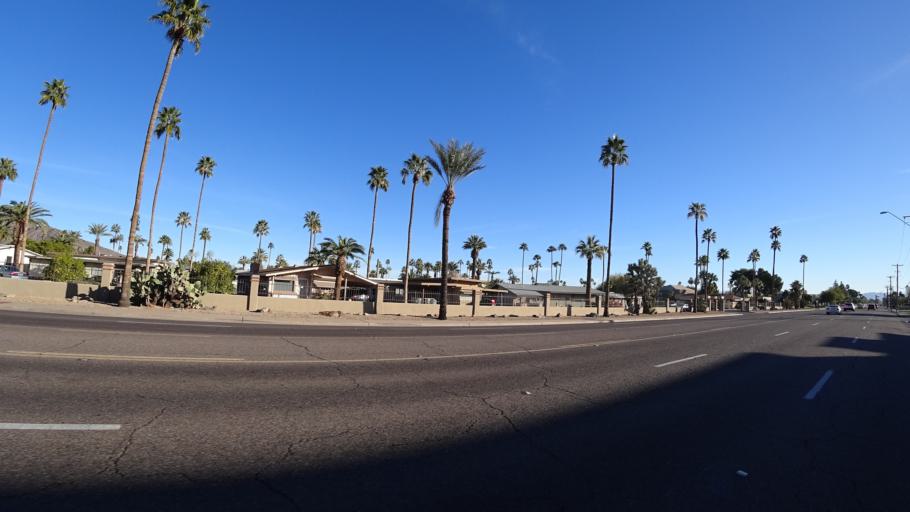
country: US
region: Arizona
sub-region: Maricopa County
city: Scottsdale
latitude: 33.4802
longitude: -111.9379
